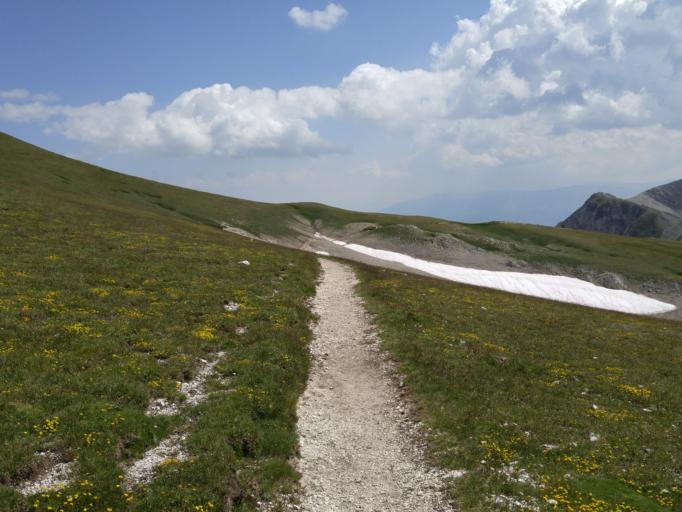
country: IT
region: Abruzzo
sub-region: Provincia di Teramo
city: Pietracamela
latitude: 42.4611
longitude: 13.5640
